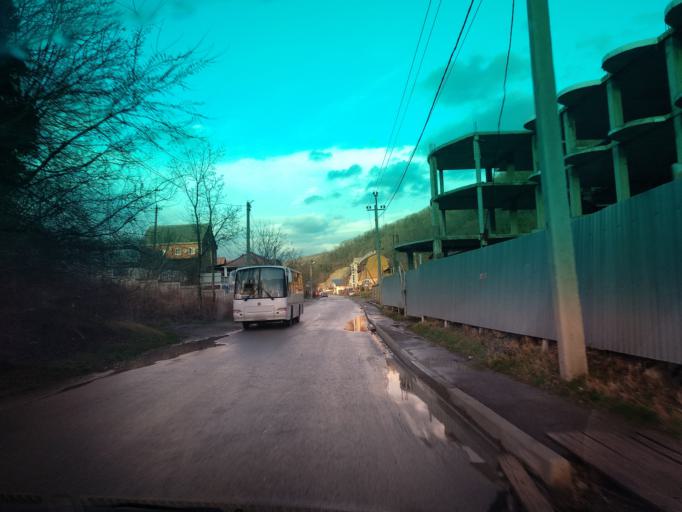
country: RU
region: Krasnodarskiy
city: Novomikhaylovskiy
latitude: 44.2649
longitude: 38.8248
